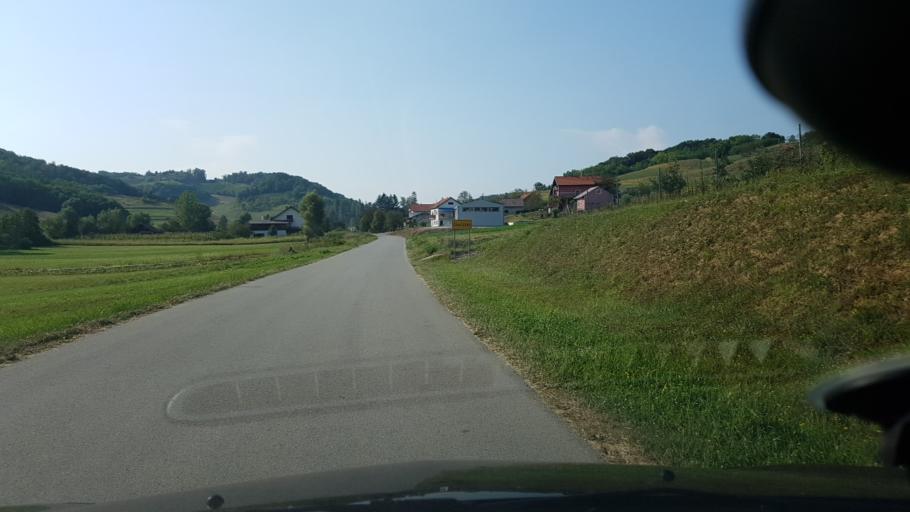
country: HR
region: Krapinsko-Zagorska
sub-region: Grad Krapina
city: Krapina
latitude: 46.1107
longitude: 15.8682
